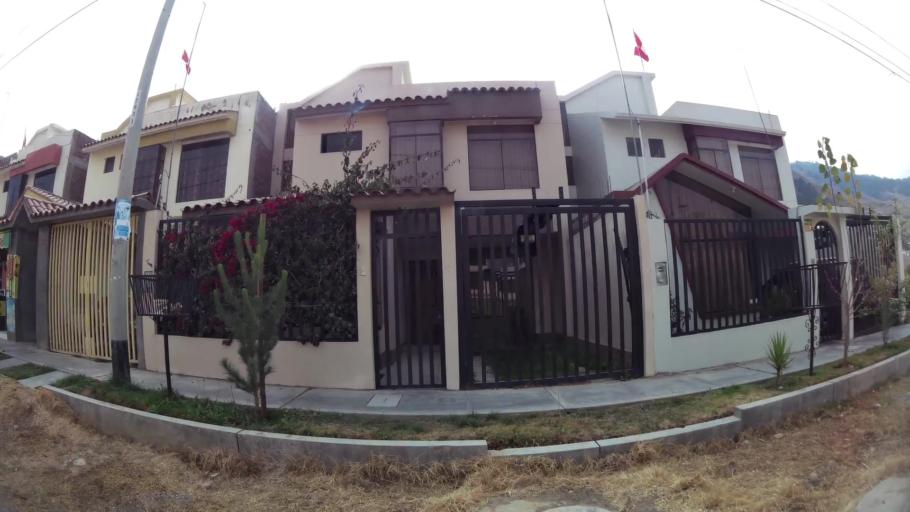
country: PE
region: Junin
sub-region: Provincia de Huancayo
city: Huancayo
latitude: -12.0473
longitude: -75.1883
